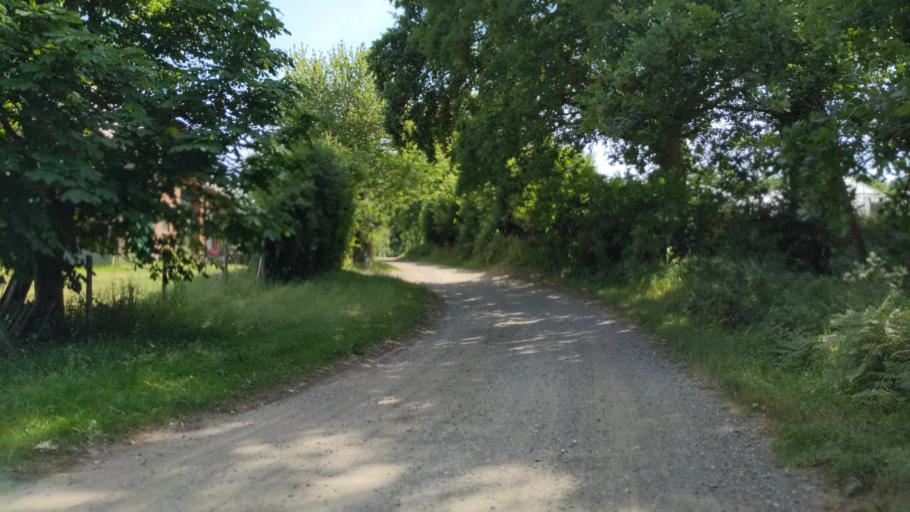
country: DE
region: Schleswig-Holstein
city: Susel
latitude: 54.0816
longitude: 10.6738
